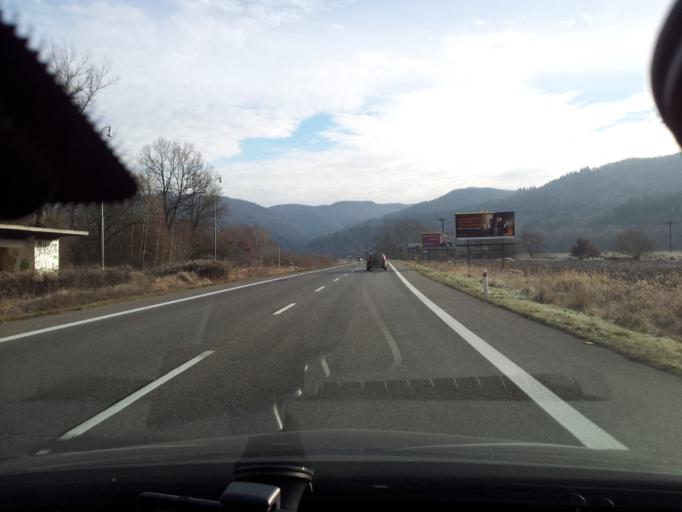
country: SK
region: Banskobystricky
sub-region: Okres Banska Bystrica
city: Banska Bystrica
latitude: 48.7464
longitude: 19.2366
